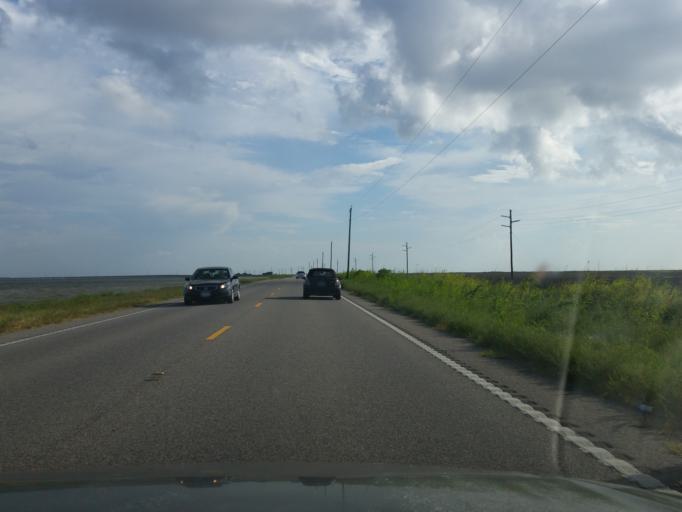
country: US
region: Alabama
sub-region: Mobile County
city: Dauphin Island
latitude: 30.3300
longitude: -88.1336
